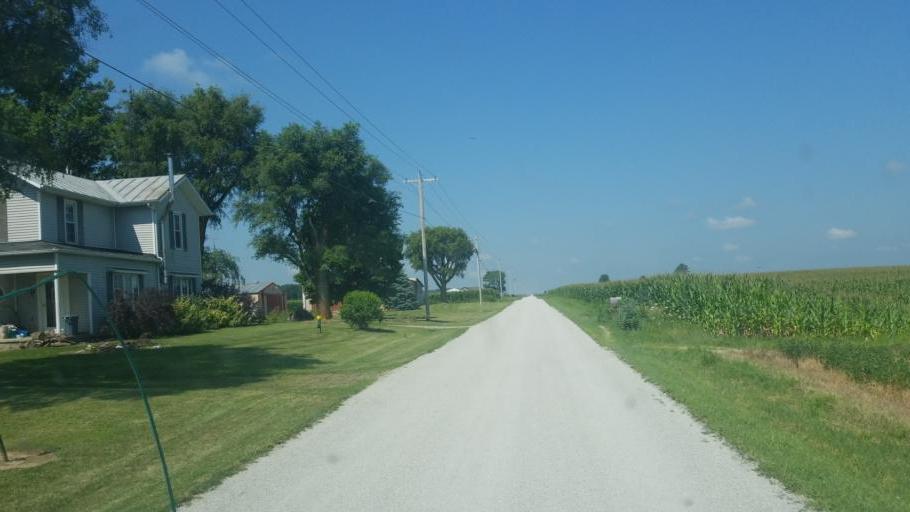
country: US
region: Ohio
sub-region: Hardin County
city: Kenton
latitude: 40.7033
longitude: -83.6786
